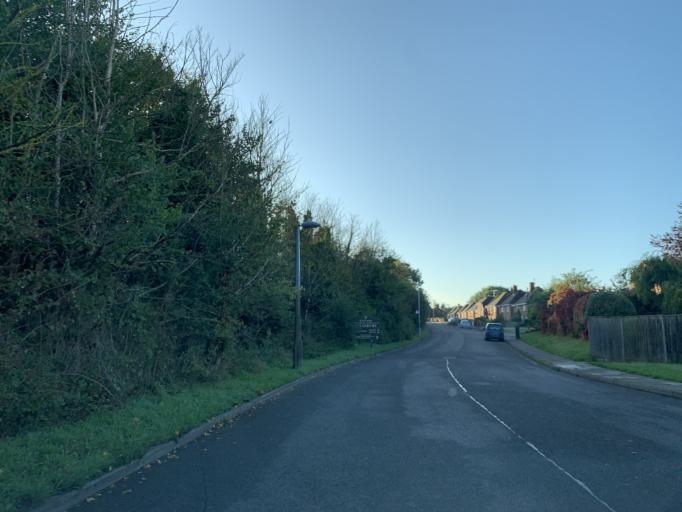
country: GB
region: England
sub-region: Wiltshire
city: Salisbury
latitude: 51.0853
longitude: -1.8050
